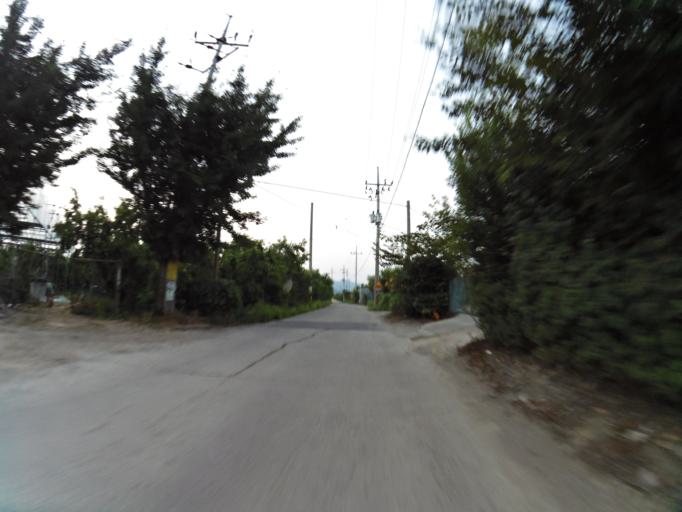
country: KR
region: Gyeongsangbuk-do
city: Gyeongsan-si
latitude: 35.8553
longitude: 128.7496
